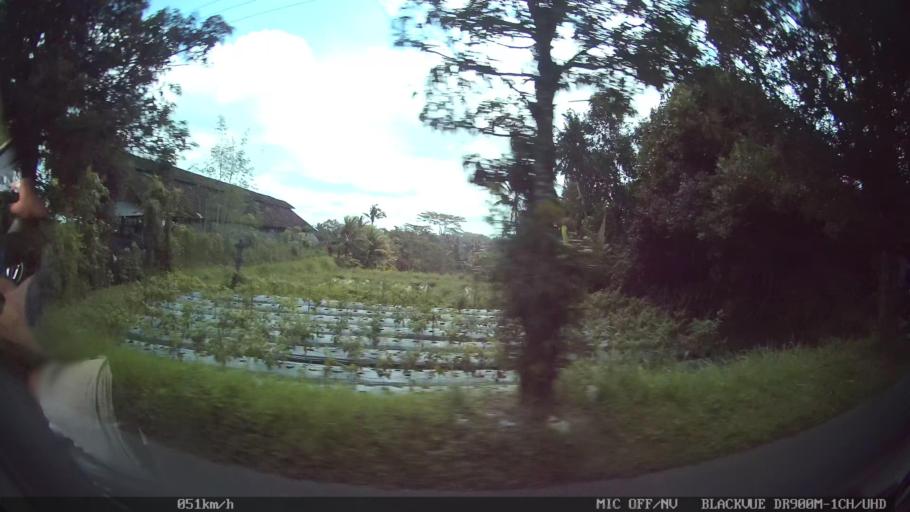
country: ID
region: Bali
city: Banjar Mulung
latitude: -8.5022
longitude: 115.3219
